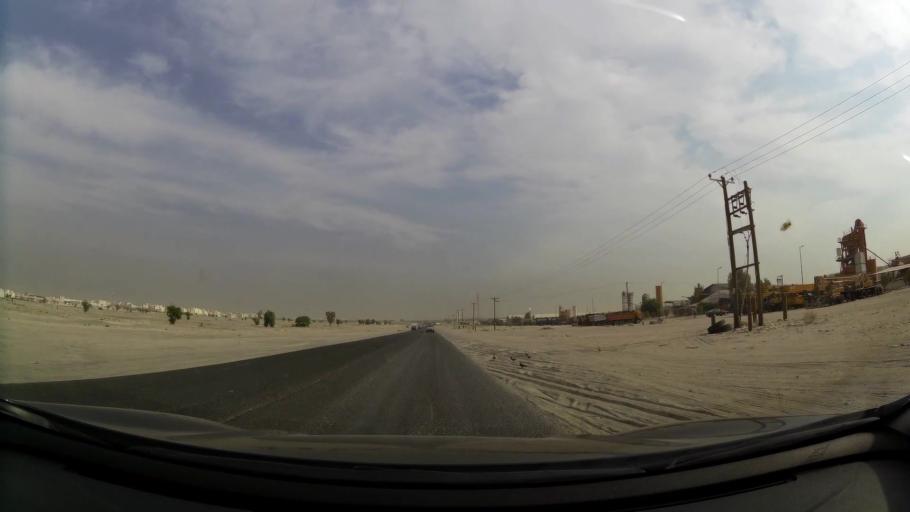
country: KW
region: Muhafazat al Jahra'
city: Al Jahra'
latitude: 29.3089
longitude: 47.7424
